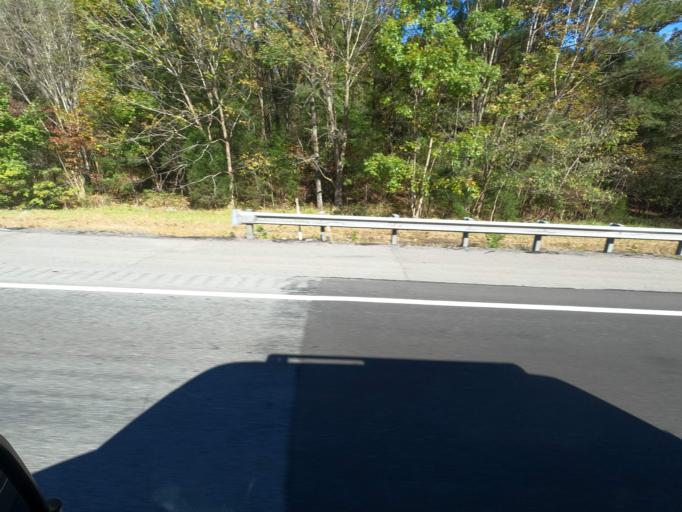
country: US
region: Tennessee
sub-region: Dickson County
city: Burns
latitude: 36.0176
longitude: -87.2453
